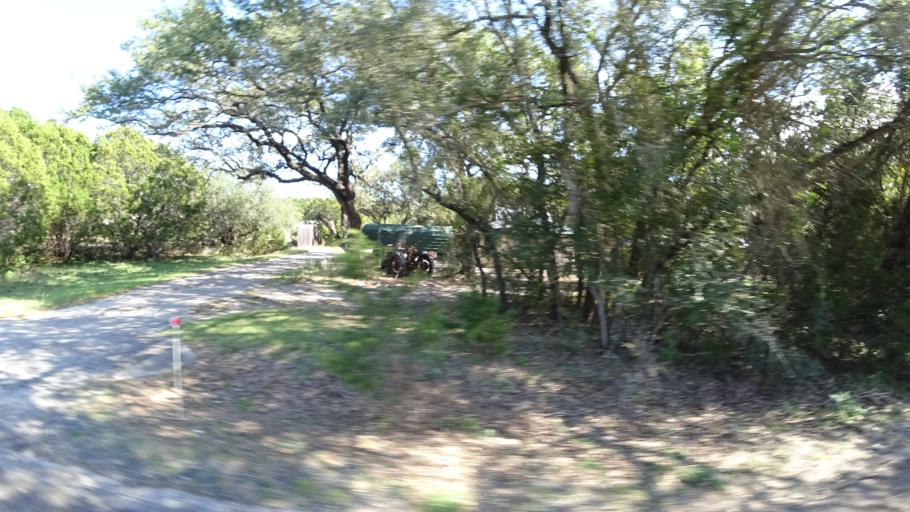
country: US
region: Texas
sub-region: Travis County
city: Barton Creek
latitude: 30.2287
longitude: -97.9146
